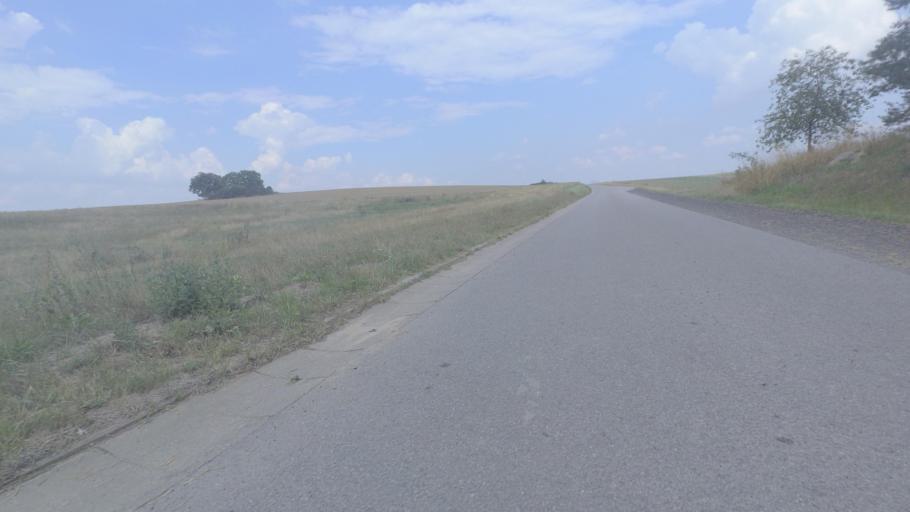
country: DE
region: Mecklenburg-Vorpommern
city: Borrentin
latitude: 53.8394
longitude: 12.9425
